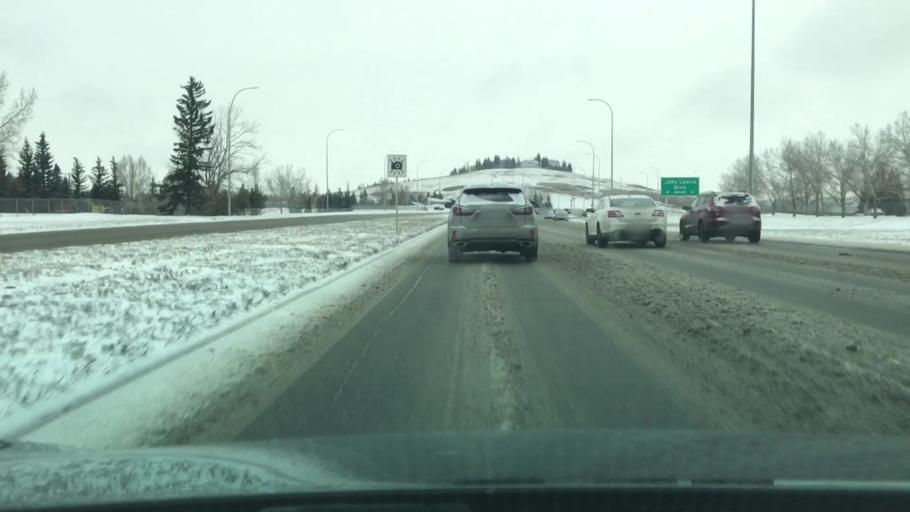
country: CA
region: Alberta
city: Calgary
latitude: 51.1061
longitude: -114.1397
